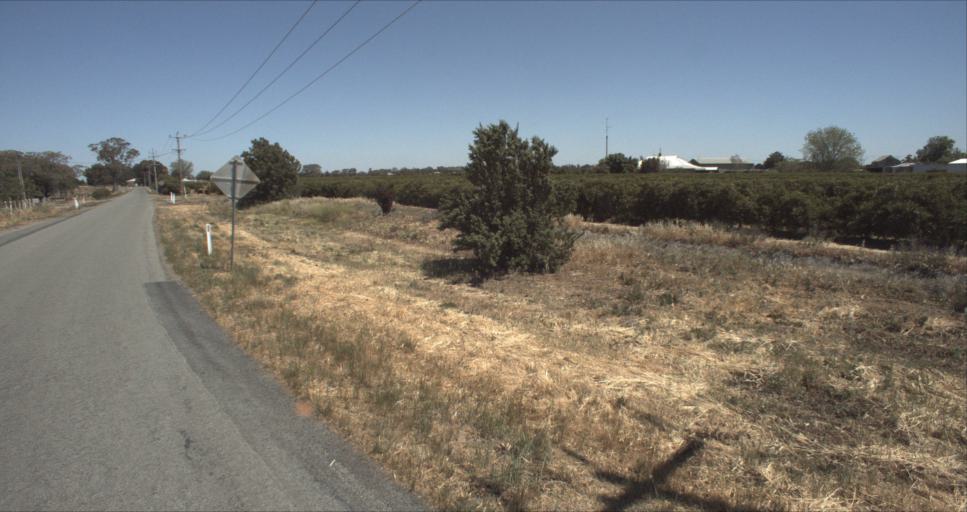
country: AU
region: New South Wales
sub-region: Leeton
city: Leeton
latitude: -34.5344
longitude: 146.3987
